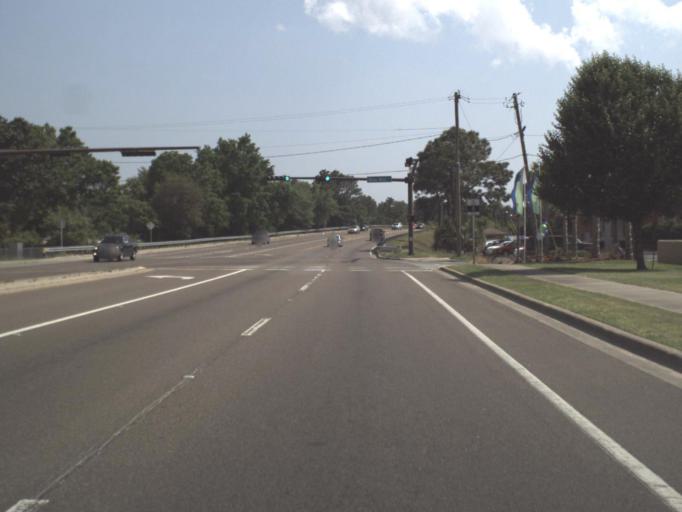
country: US
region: Florida
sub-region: Escambia County
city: Ferry Pass
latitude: 30.5050
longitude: -87.1841
